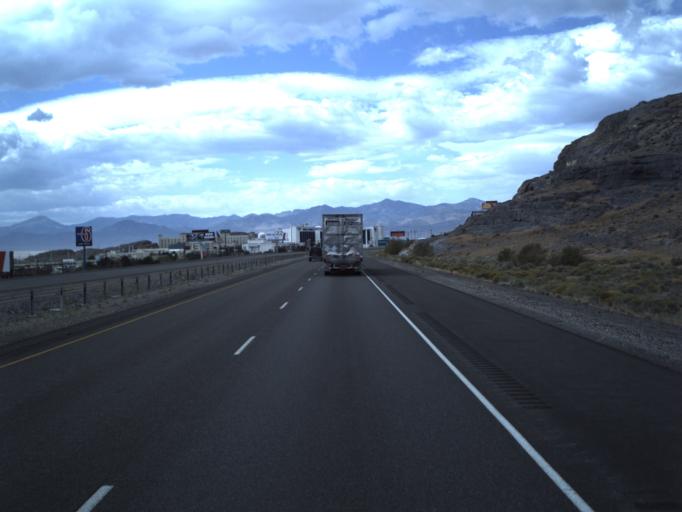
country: US
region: Utah
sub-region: Tooele County
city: Wendover
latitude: 40.7407
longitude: -114.0339
